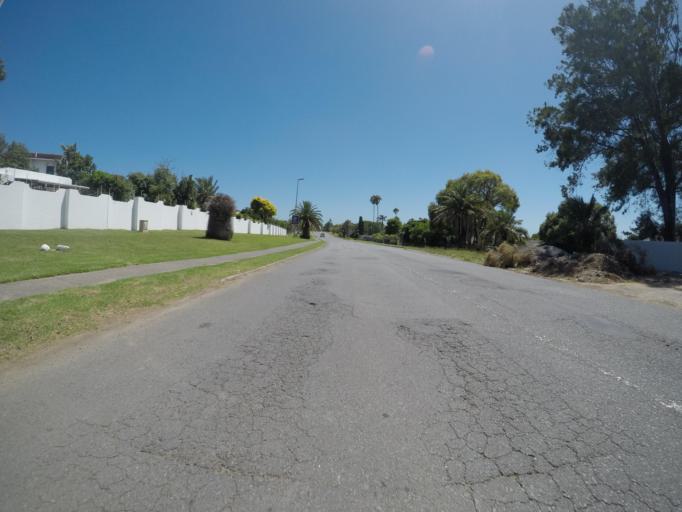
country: ZA
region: Eastern Cape
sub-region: Buffalo City Metropolitan Municipality
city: East London
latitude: -32.9749
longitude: 27.9411
